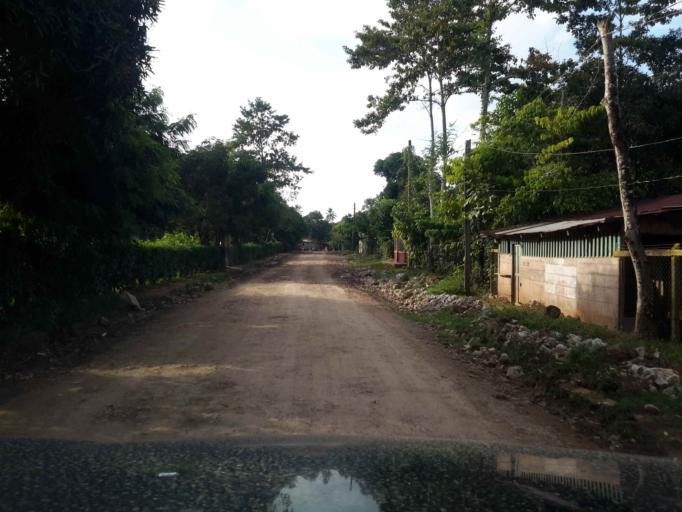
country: CR
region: Alajuela
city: Los Chiles
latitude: 11.1546
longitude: -84.6281
